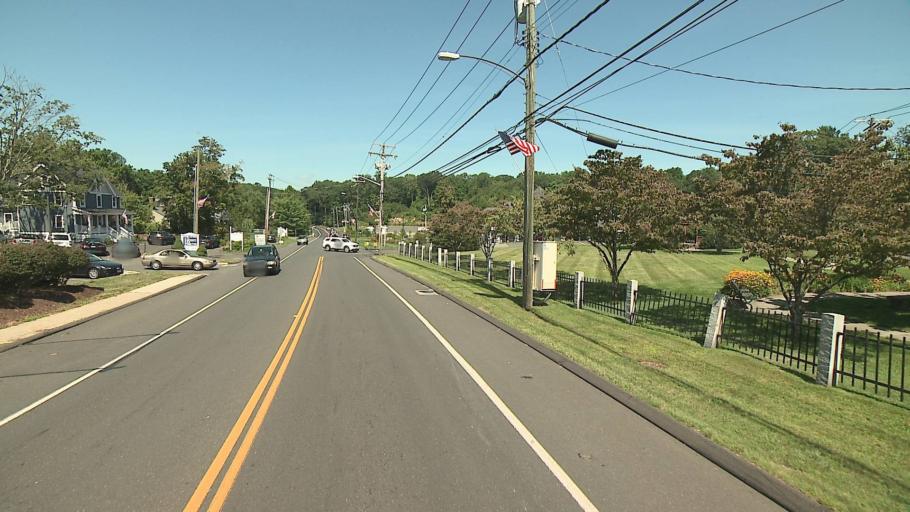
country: US
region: Connecticut
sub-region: Fairfield County
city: Trumbull
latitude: 41.2776
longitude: -73.2275
